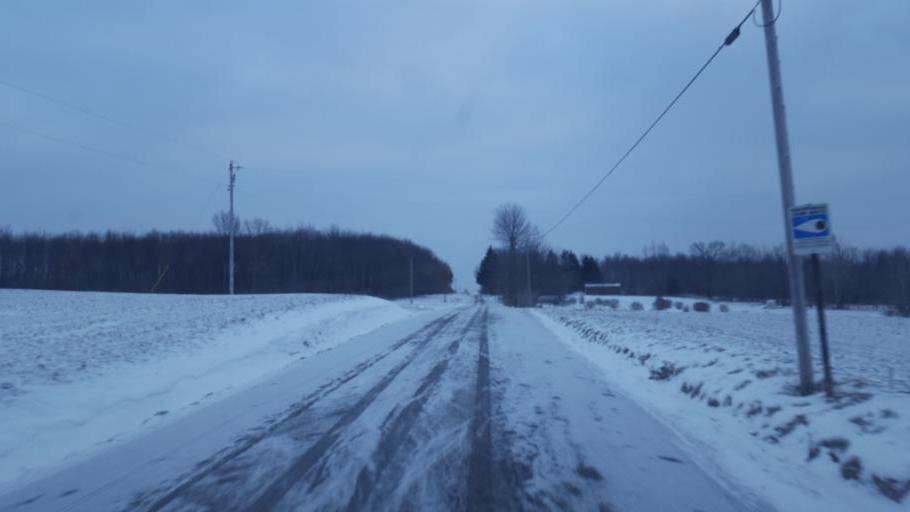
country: US
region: Pennsylvania
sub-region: Crawford County
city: Cochranton
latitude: 41.4332
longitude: -79.9992
